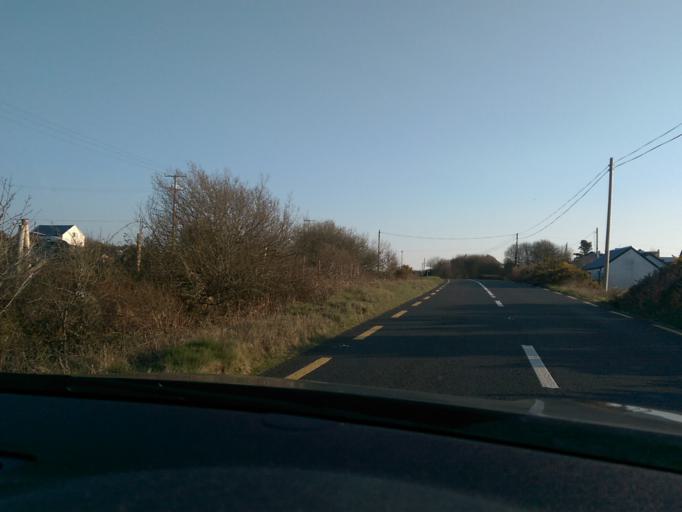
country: IE
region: Connaught
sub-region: County Galway
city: Oughterard
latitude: 53.3429
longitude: -9.5454
